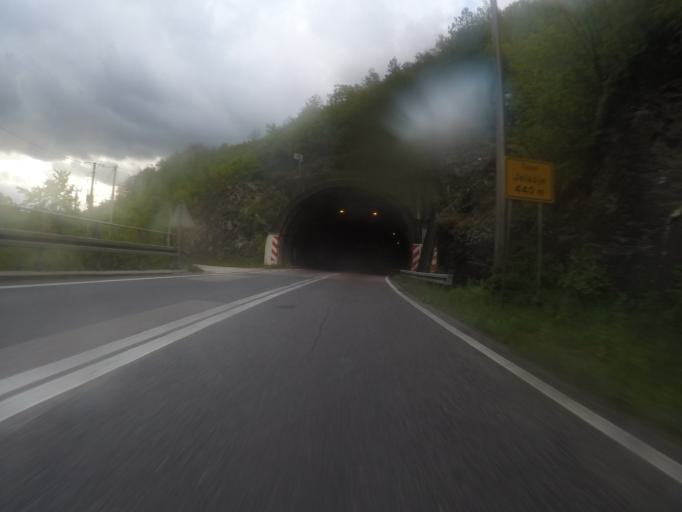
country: BA
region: Federation of Bosnia and Herzegovina
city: Jablanica
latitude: 43.6776
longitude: 17.7755
